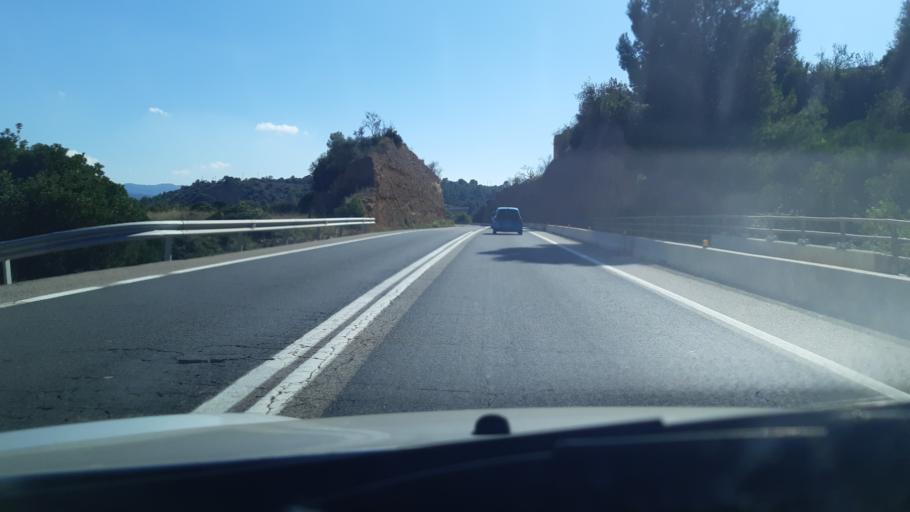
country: ES
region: Catalonia
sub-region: Provincia de Tarragona
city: Tivenys
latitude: 40.8873
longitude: 0.4916
